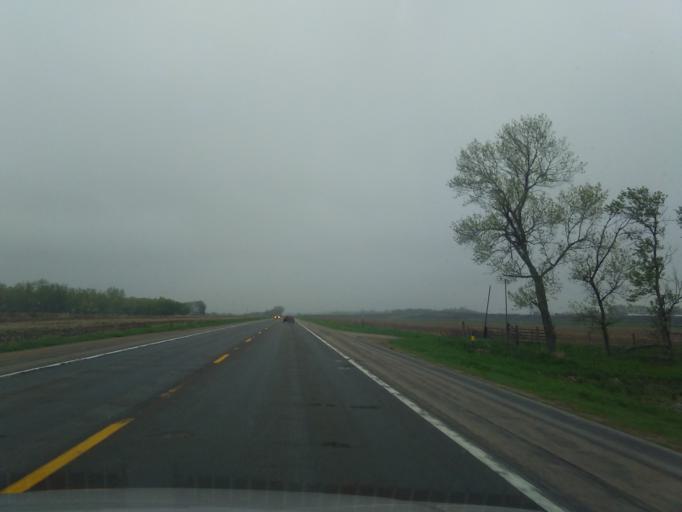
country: US
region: Nebraska
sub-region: Cuming County
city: Wisner
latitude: 41.9414
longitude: -96.8360
